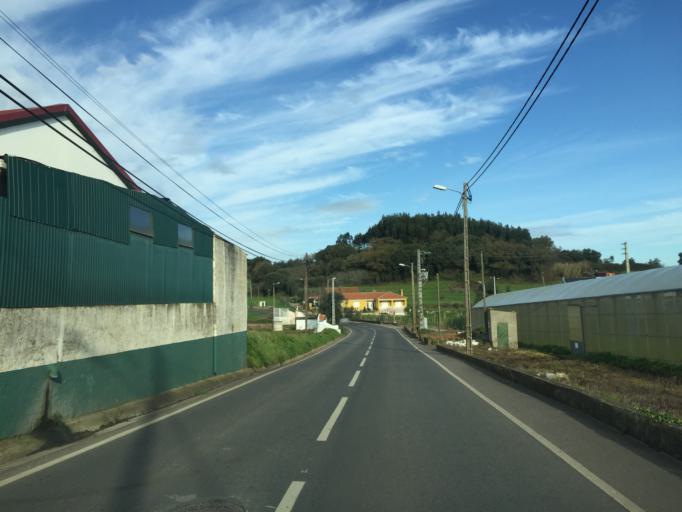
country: PT
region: Lisbon
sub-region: Sintra
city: Almargem
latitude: 38.8422
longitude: -9.2577
